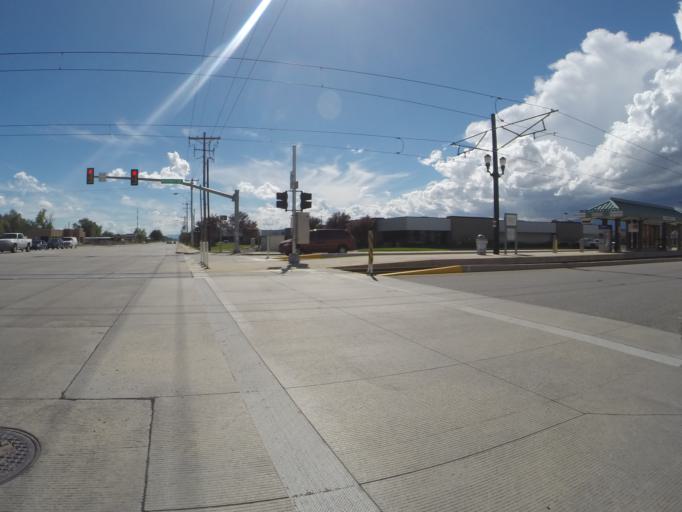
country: US
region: Utah
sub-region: Salt Lake County
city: Taylorsville
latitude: 40.7113
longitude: -111.9391
